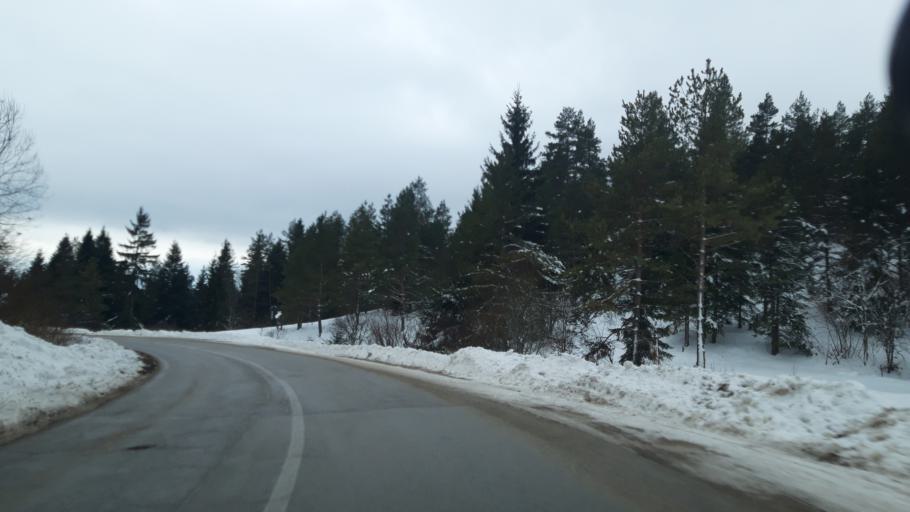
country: BA
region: Republika Srpska
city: Han Pijesak
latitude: 44.0246
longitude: 18.8822
